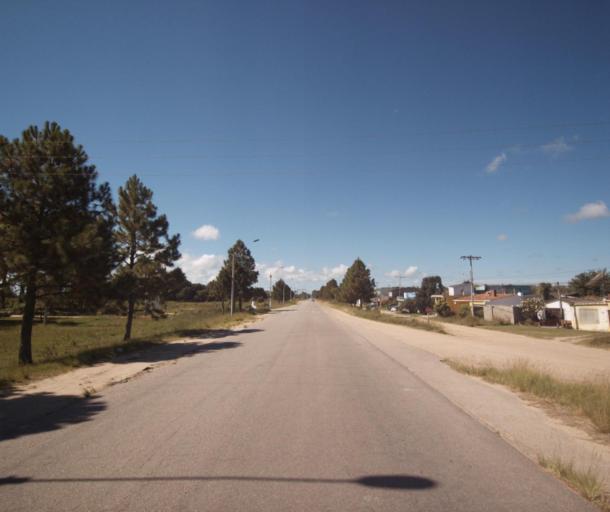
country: BR
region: Rio Grande do Sul
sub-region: Chui
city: Chui
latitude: -33.6878
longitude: -53.4540
